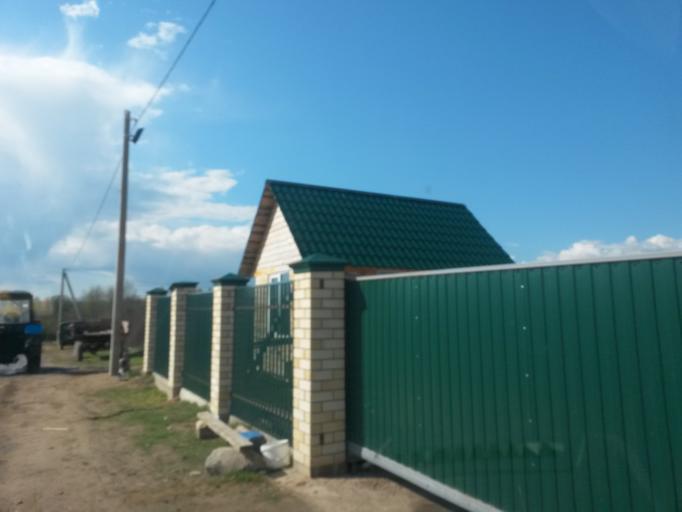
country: RU
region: Jaroslavl
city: Tutayev
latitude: 57.9464
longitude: 39.4378
